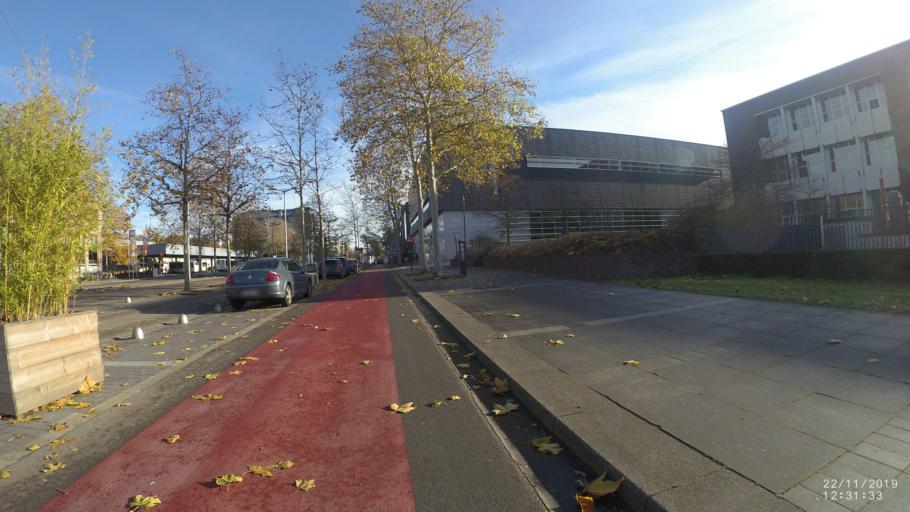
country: BE
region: Flanders
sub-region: Provincie Limburg
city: Genk
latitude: 50.9662
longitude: 5.4943
